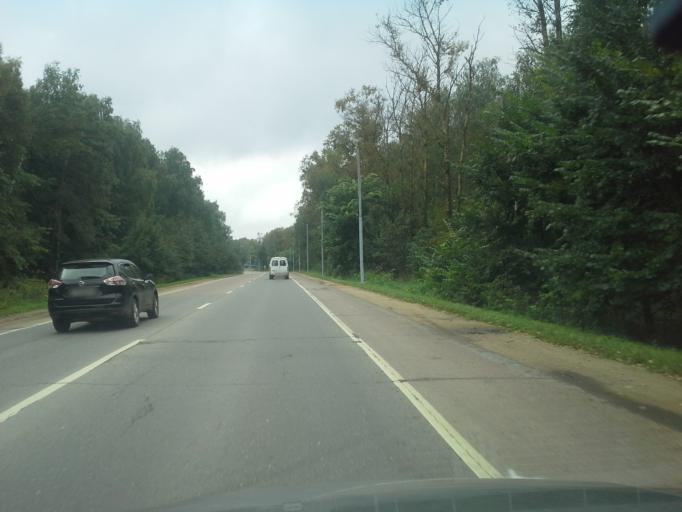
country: RU
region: Moskovskaya
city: Chupryakovo
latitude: 55.5731
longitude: 36.6447
